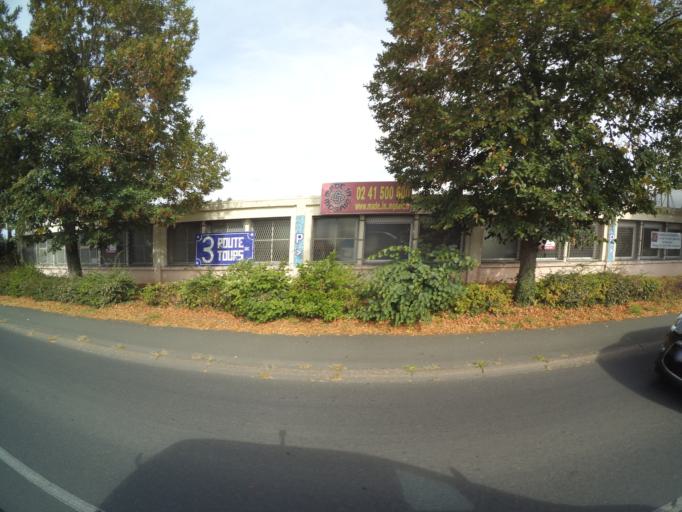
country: FR
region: Pays de la Loire
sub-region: Departement de Maine-et-Loire
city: Saumur
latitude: 47.2653
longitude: -0.0654
